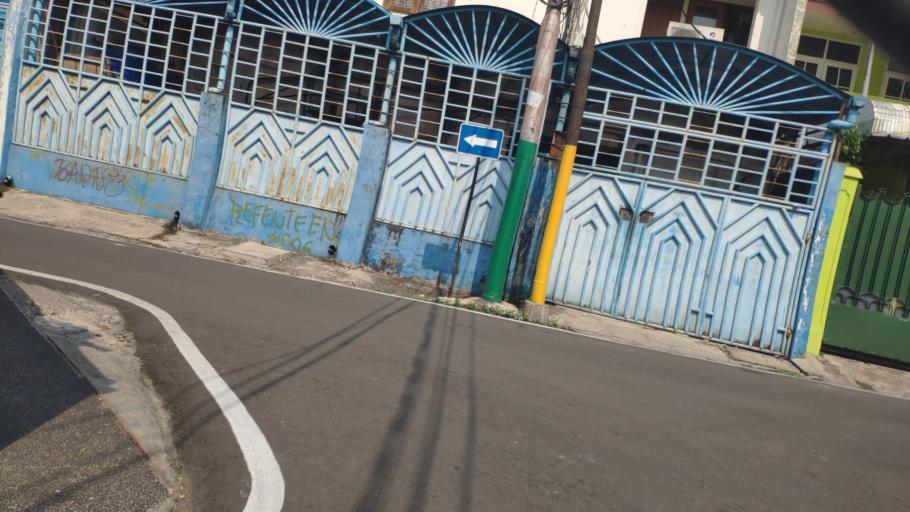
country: ID
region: Jakarta Raya
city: Jakarta
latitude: -6.2518
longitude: 106.7968
